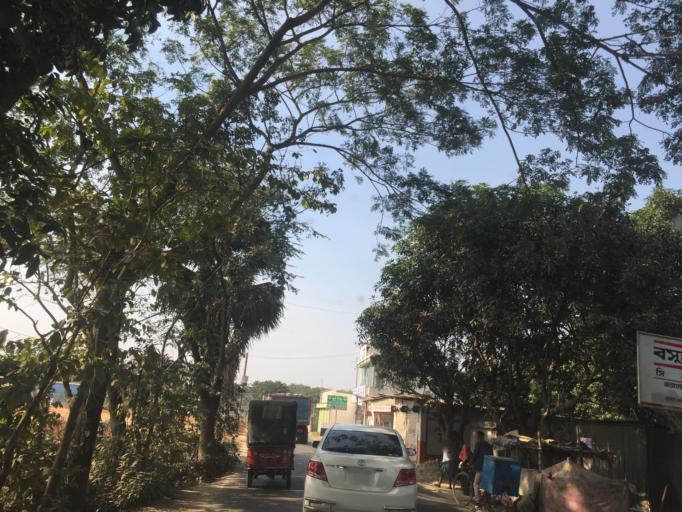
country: BD
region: Dhaka
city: Tungi
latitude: 23.8570
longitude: 90.3277
